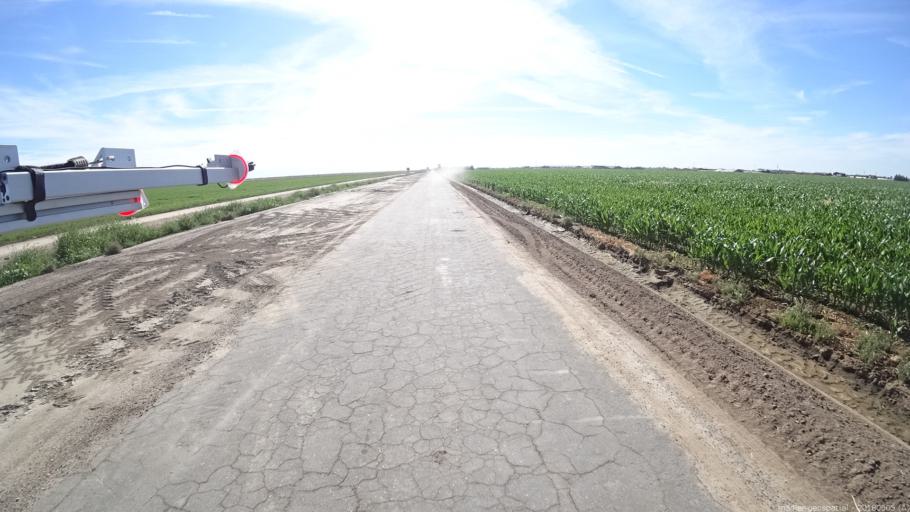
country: US
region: California
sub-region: Madera County
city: Chowchilla
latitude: 37.1417
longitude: -120.2968
